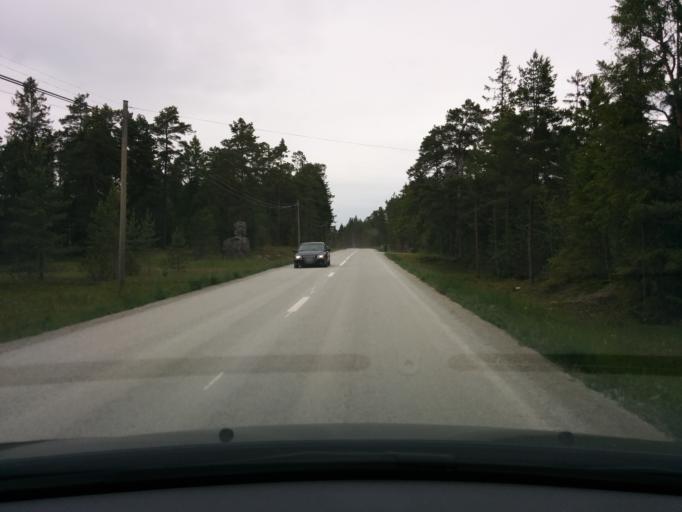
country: SE
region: Gotland
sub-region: Gotland
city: Slite
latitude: 57.6161
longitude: 18.7573
